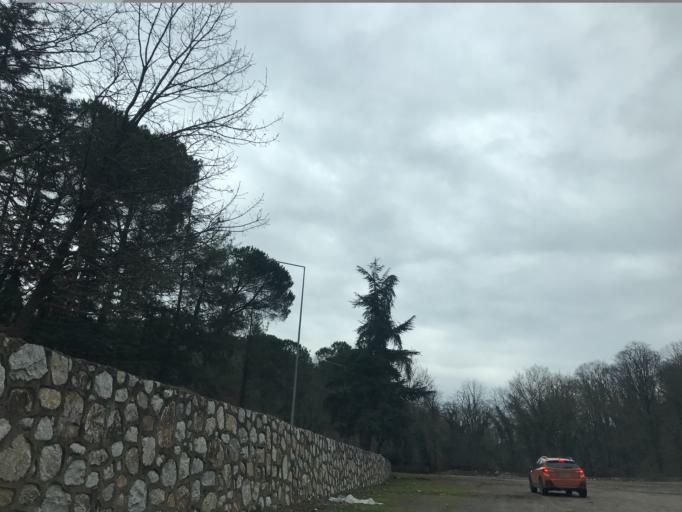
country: TR
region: Yalova
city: Termal
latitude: 40.6020
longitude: 29.1776
